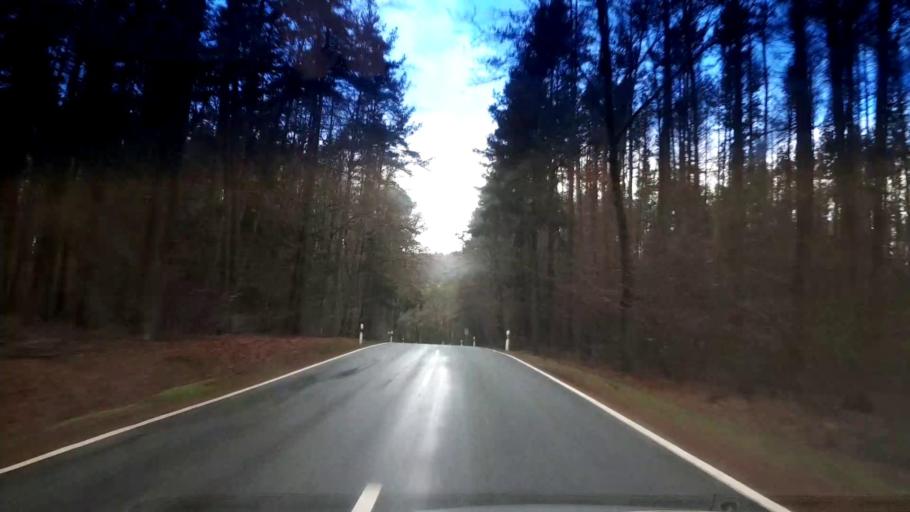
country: DE
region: Bavaria
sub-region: Upper Franconia
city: Lauter
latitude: 49.9661
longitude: 10.7605
